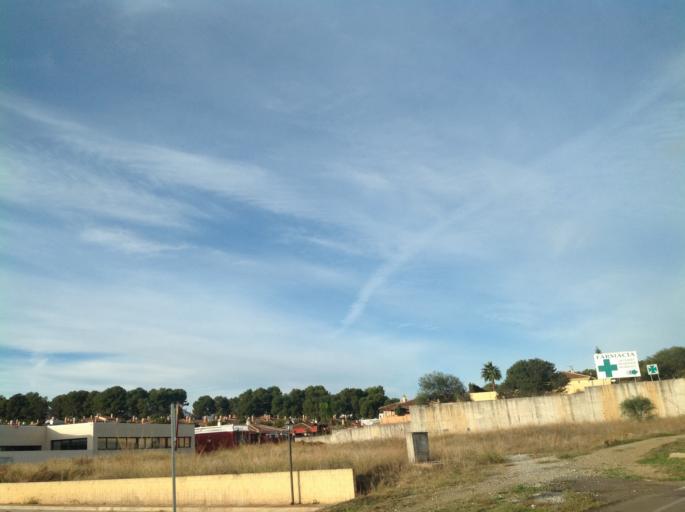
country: ES
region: Andalusia
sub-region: Provincia de Malaga
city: Pizarra
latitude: 36.7485
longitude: -4.7167
